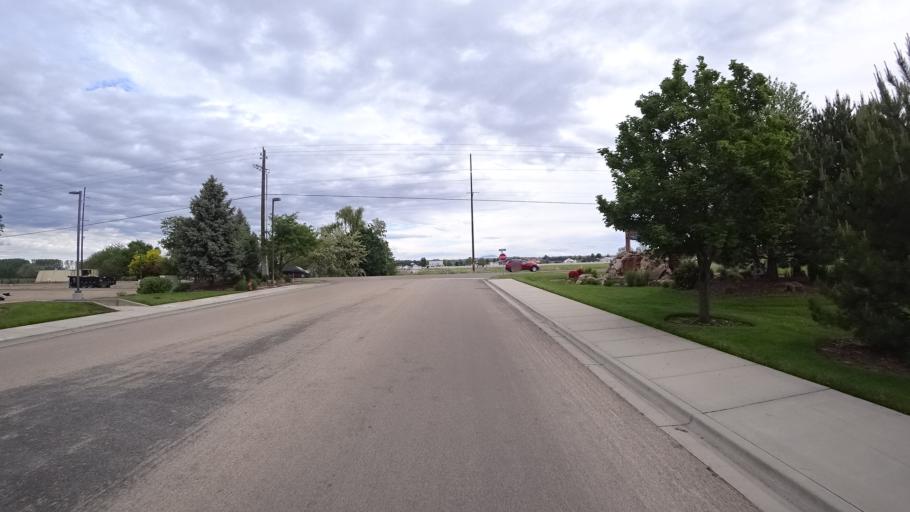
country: US
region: Idaho
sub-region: Ada County
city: Star
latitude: 43.6919
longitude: -116.5034
